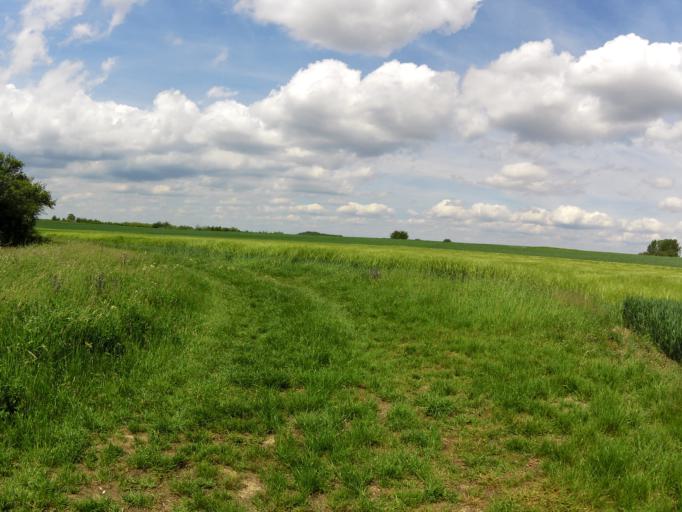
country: DE
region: Bavaria
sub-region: Regierungsbezirk Unterfranken
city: Sommerhausen
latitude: 49.7252
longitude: 10.0365
